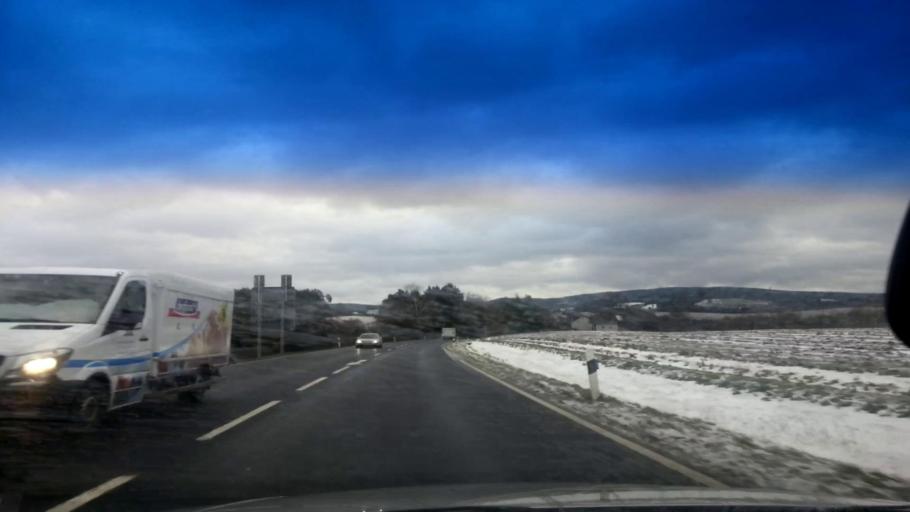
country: DE
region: Bavaria
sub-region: Upper Franconia
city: Gefrees
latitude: 50.0959
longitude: 11.6994
